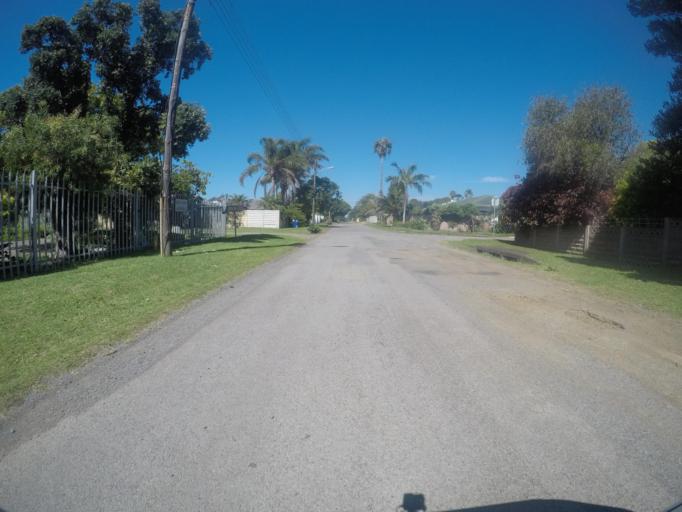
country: ZA
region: Eastern Cape
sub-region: Buffalo City Metropolitan Municipality
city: East London
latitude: -32.9489
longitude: 28.0070
